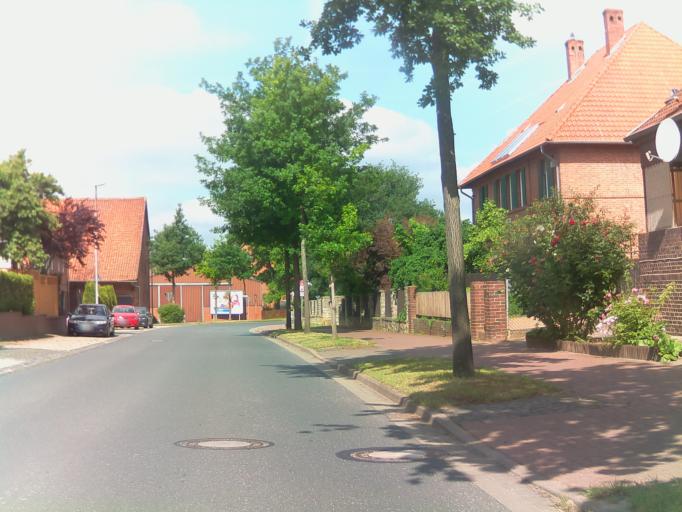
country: DE
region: Lower Saxony
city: Harsum
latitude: 52.2111
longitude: 9.9610
